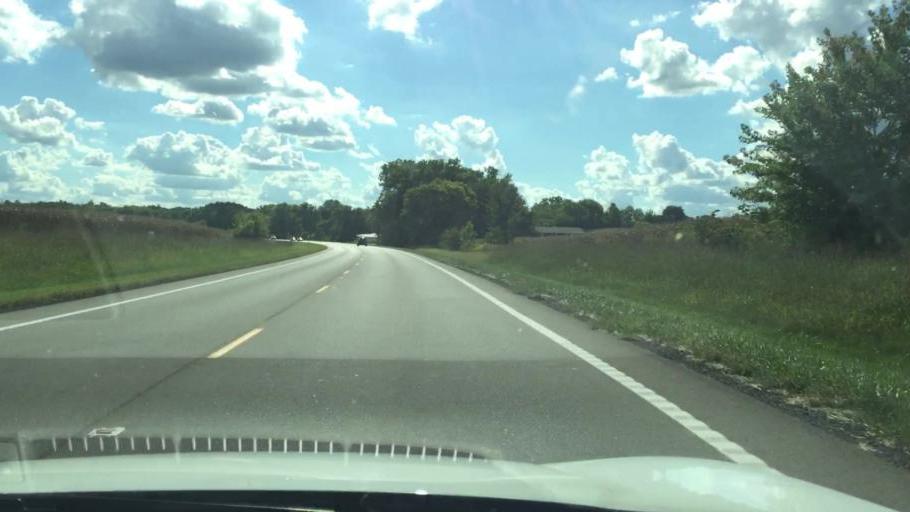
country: US
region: Ohio
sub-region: Clark County
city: Northridge
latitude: 40.0026
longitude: -83.7203
